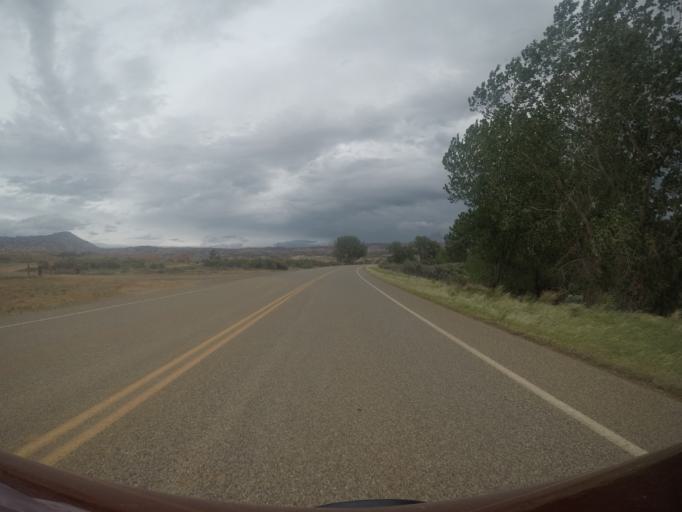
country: US
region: Wyoming
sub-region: Big Horn County
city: Lovell
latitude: 44.9629
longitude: -108.2829
